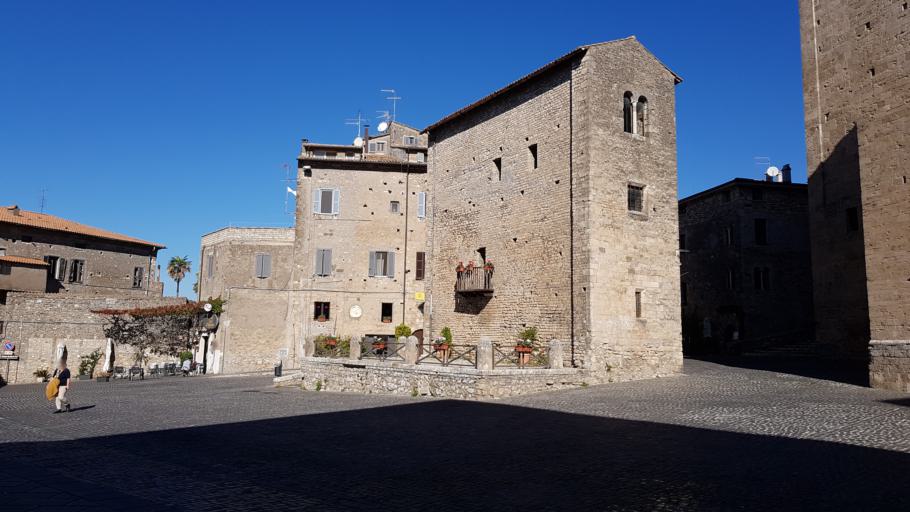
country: IT
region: Latium
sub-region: Provincia di Frosinone
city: Anagni
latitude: 41.7426
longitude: 13.1617
